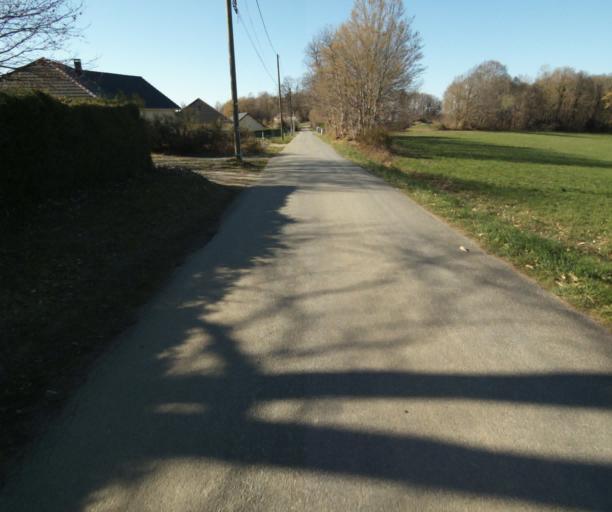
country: FR
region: Limousin
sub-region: Departement de la Correze
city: Seilhac
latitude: 45.3893
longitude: 1.7082
